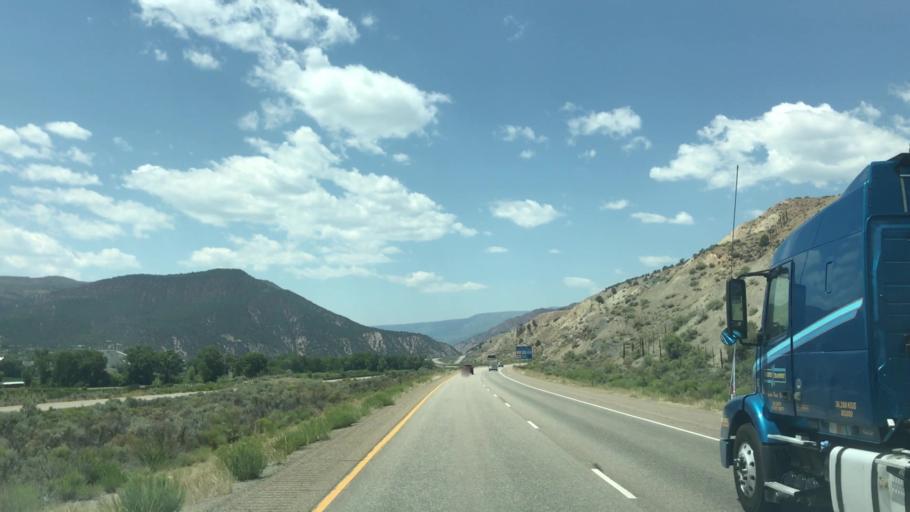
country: US
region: Colorado
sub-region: Eagle County
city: Gypsum
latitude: 39.6540
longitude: -106.9325
